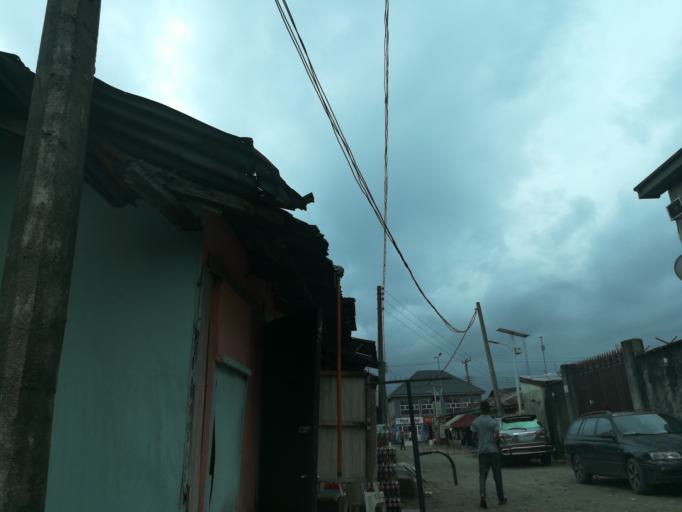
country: NG
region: Rivers
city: Port Harcourt
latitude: 4.8415
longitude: 7.0384
